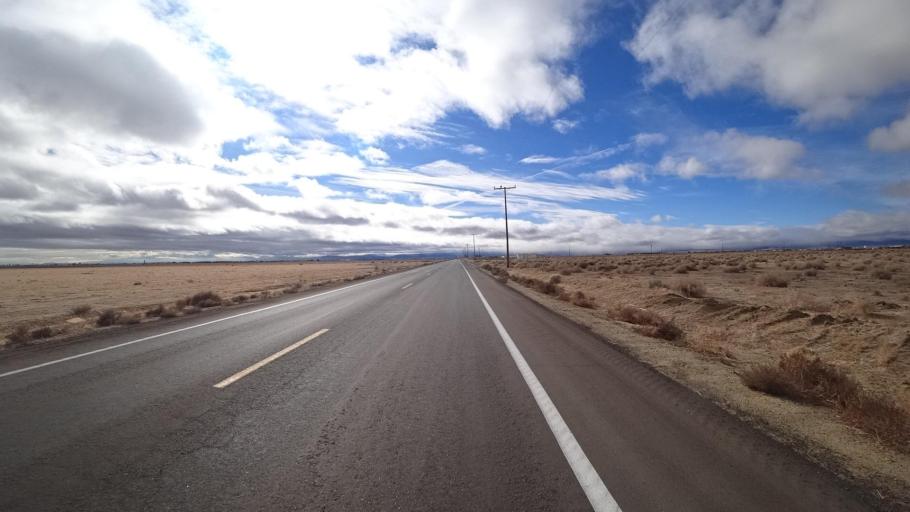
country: US
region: California
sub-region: Kern County
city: Rosamond
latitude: 34.8489
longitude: -118.2909
